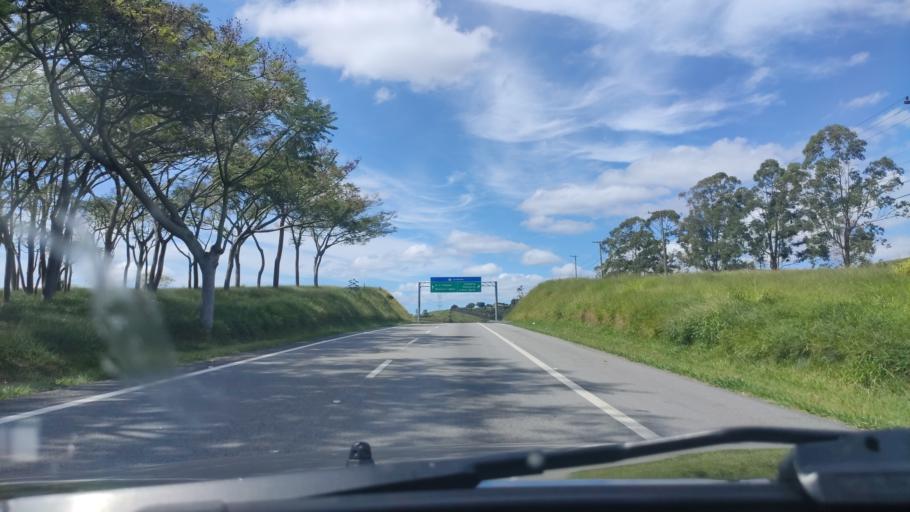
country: BR
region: Sao Paulo
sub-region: Sao Jose Dos Campos
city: Sao Jose dos Campos
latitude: -23.2697
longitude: -45.8236
